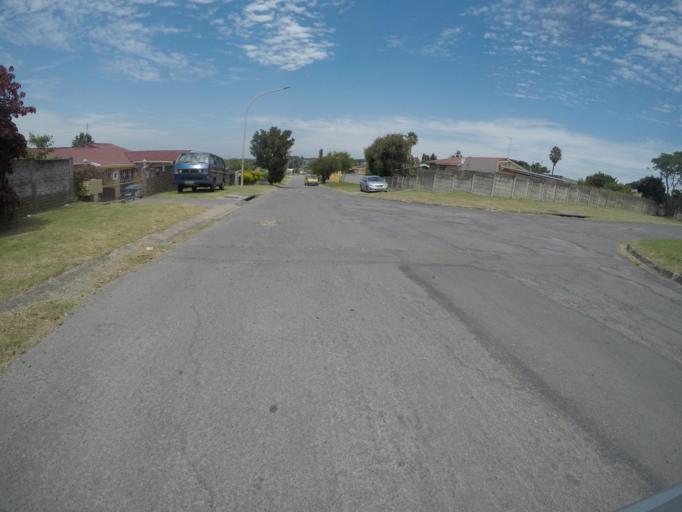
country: ZA
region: Eastern Cape
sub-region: Buffalo City Metropolitan Municipality
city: East London
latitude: -32.9780
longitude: 27.8640
